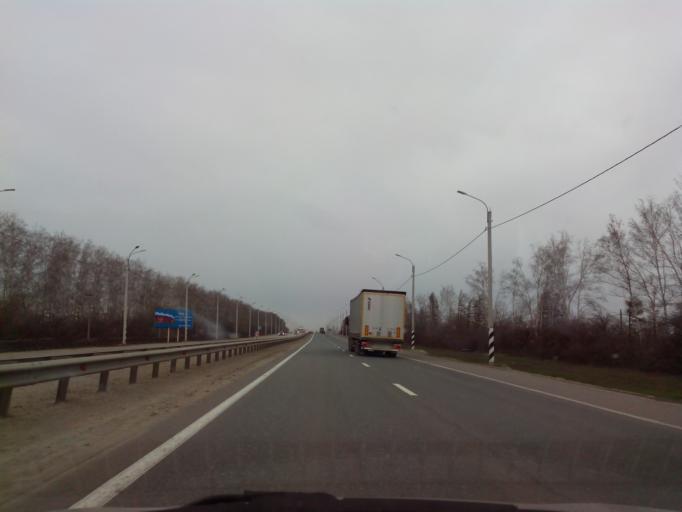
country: RU
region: Tambov
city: Komsomolets
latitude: 52.7359
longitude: 41.2706
